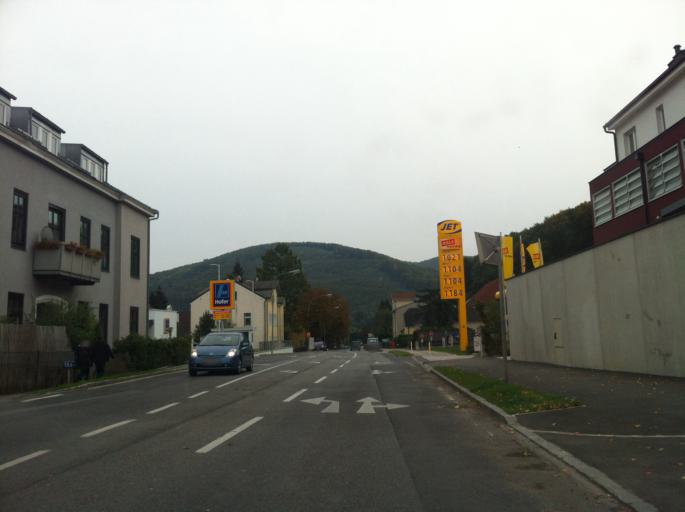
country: AT
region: Lower Austria
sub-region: Politischer Bezirk Wien-Umgebung
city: Purkersdorf
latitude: 48.2147
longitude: 16.1702
